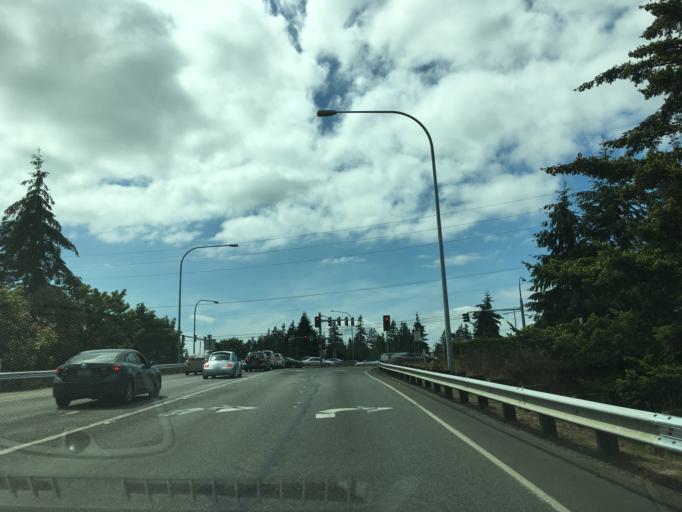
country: US
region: Washington
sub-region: Snohomish County
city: Everett
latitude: 47.9232
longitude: -122.2253
